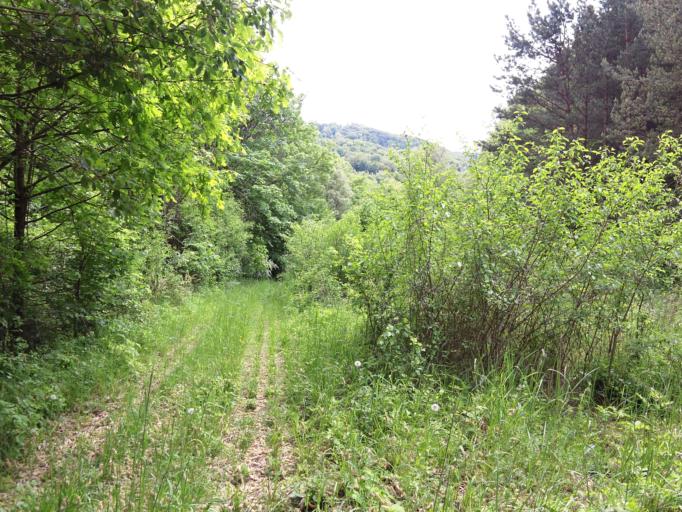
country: DE
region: Thuringia
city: Ifta
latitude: 51.0637
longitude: 10.1476
